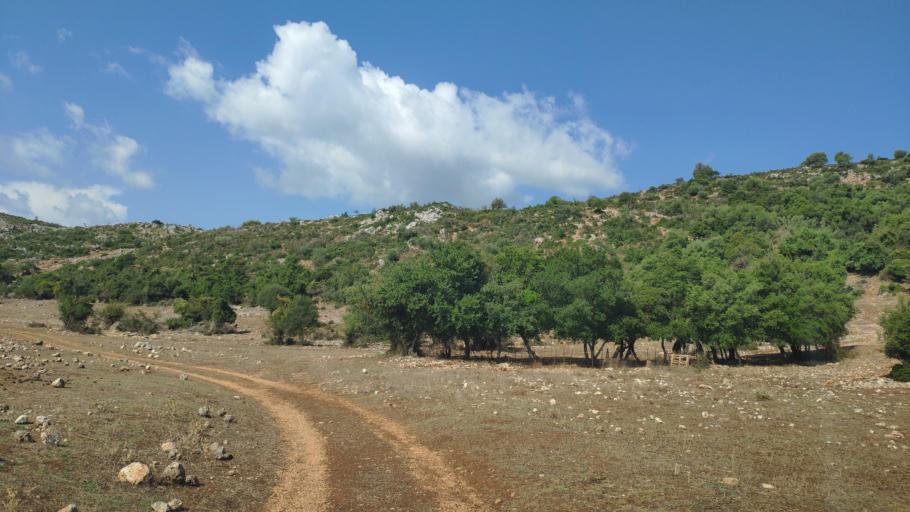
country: GR
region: West Greece
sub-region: Nomos Aitolias kai Akarnanias
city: Fitiai
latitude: 38.6815
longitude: 21.1430
